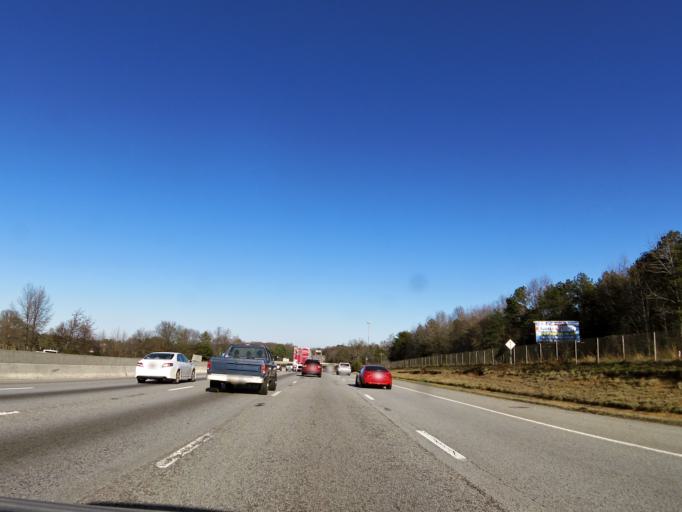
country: US
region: South Carolina
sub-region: Greenville County
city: Mauldin
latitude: 34.8357
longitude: -82.2924
